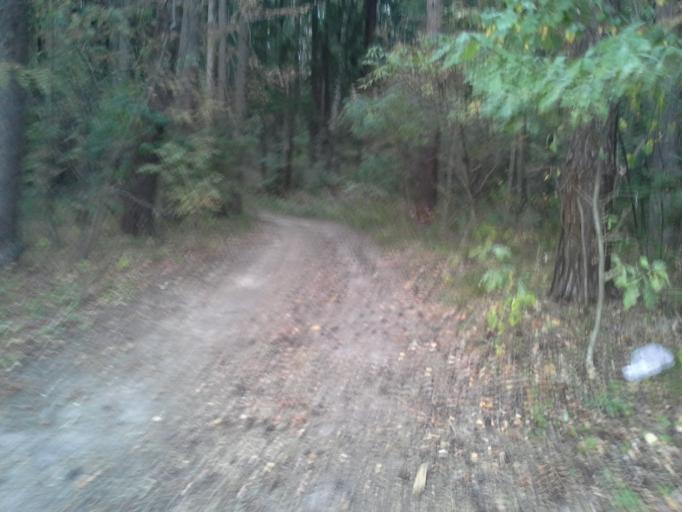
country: RU
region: Moskovskaya
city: Aprelevka
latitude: 55.5470
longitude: 37.0340
